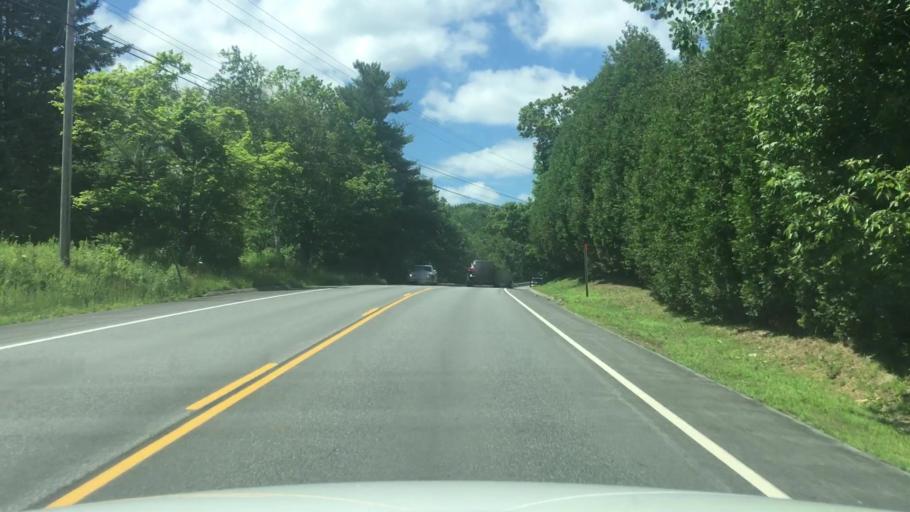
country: US
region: Maine
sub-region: Waldo County
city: Searsmont
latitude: 44.3996
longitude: -69.1191
